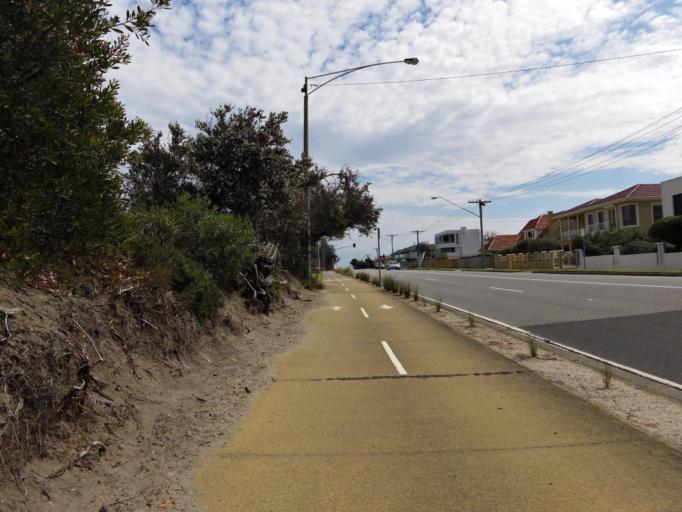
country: AU
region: Victoria
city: Beaumaris
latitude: -37.9950
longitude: 145.0360
